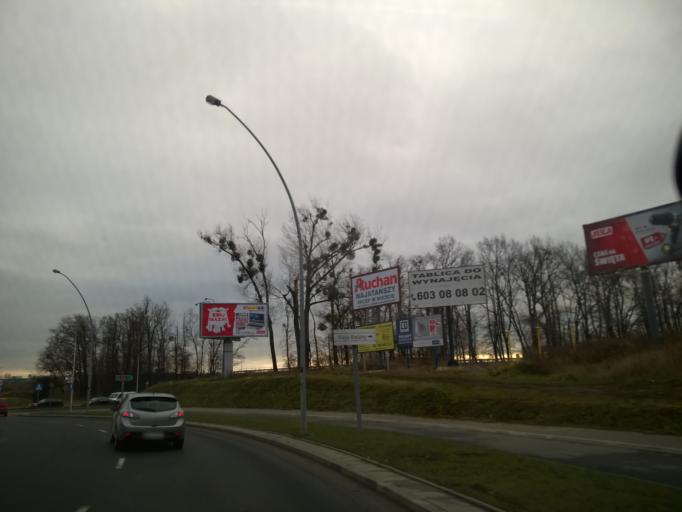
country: PL
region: Lower Silesian Voivodeship
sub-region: Powiat wroclawski
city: Bielany Wroclawskie
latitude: 51.0516
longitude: 16.9640
